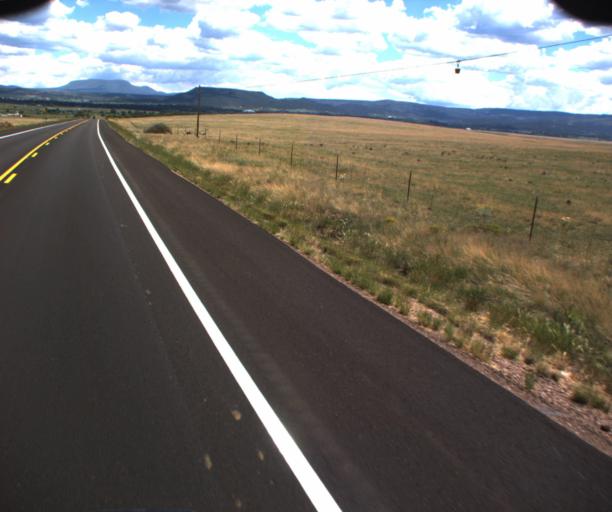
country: US
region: Arizona
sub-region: Apache County
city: Springerville
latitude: 34.1672
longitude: -109.3102
